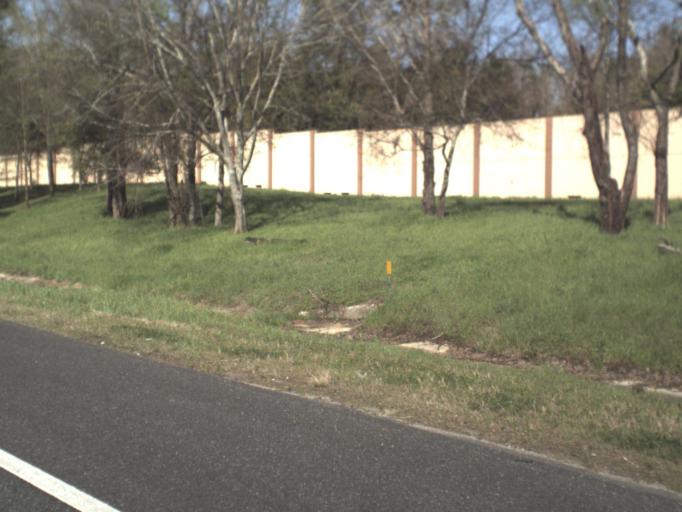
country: US
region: Florida
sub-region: Leon County
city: Tallahassee
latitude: 30.4803
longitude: -84.3194
